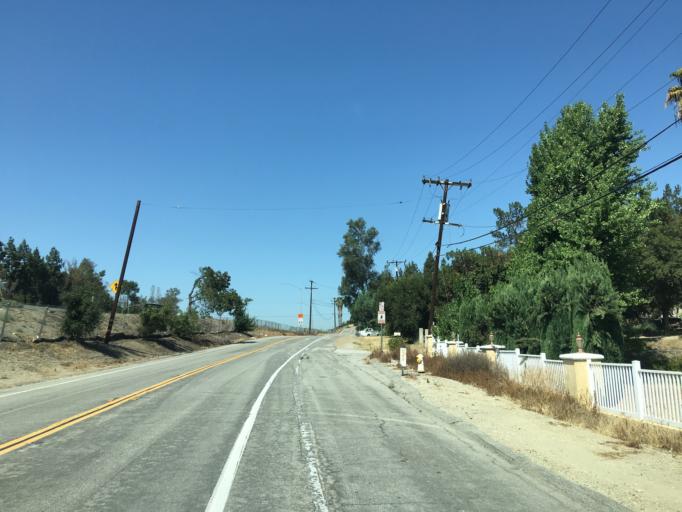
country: US
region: California
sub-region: Los Angeles County
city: Charter Oak
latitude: 34.0695
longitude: -117.8404
